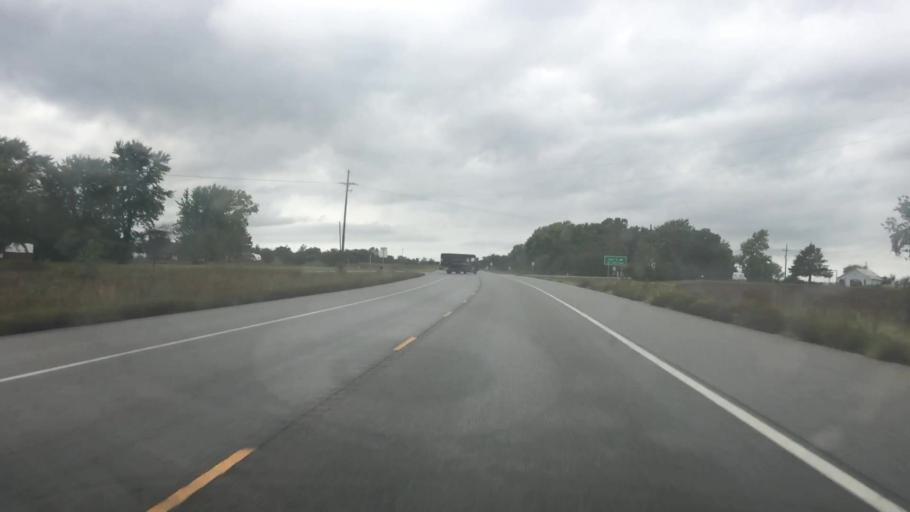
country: US
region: Kansas
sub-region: Miami County
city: Osawatomie
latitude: 38.4412
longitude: -94.9964
